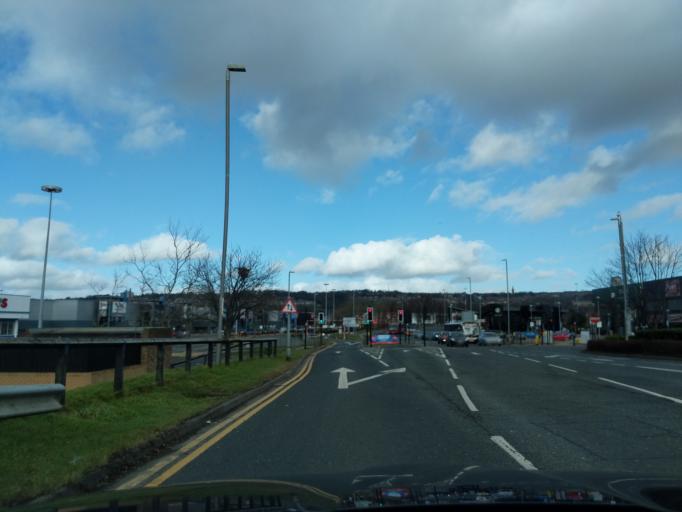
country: GB
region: England
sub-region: Gateshead
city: Whickham
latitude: 54.9581
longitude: -1.6748
